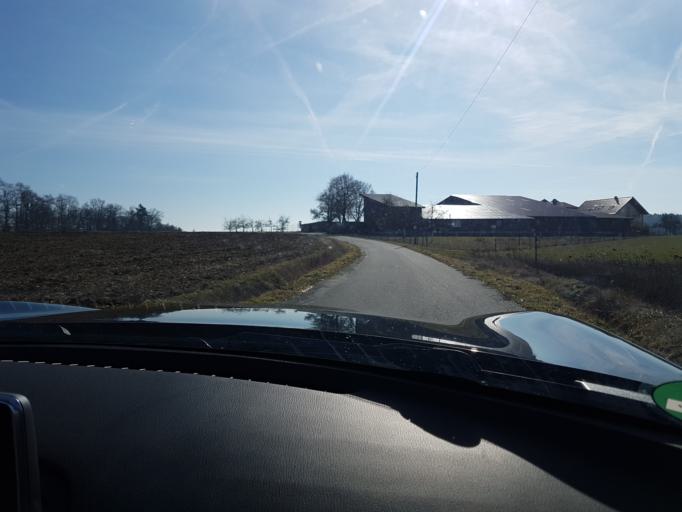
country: DE
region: Baden-Wuerttemberg
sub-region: Karlsruhe Region
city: Rosenberg
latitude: 49.4421
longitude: 9.4837
